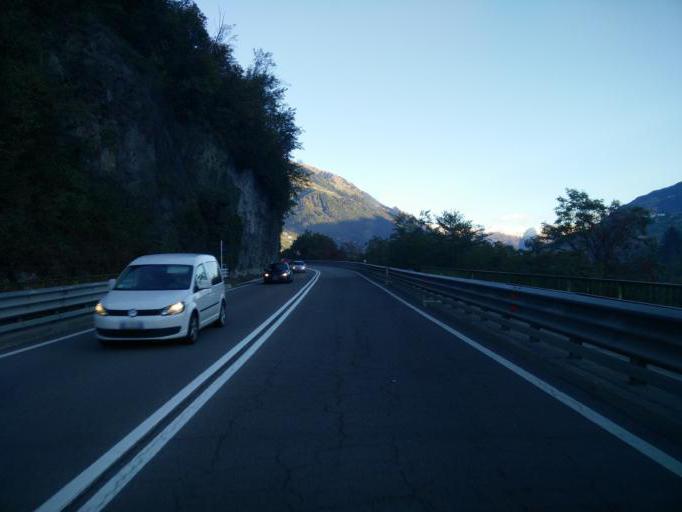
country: IT
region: Trentino-Alto Adige
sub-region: Bolzano
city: Merano
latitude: 46.6739
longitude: 11.1729
